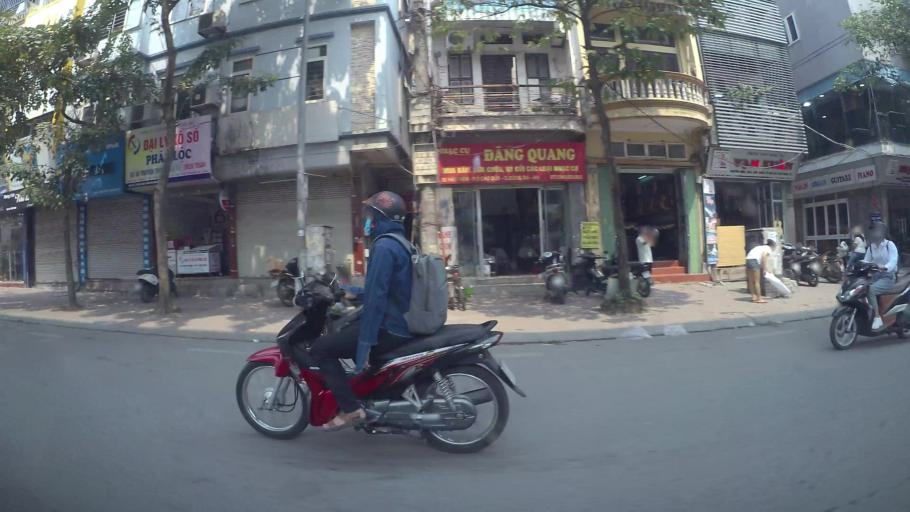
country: VN
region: Ha Noi
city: Dong Da
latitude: 21.0220
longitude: 105.8261
